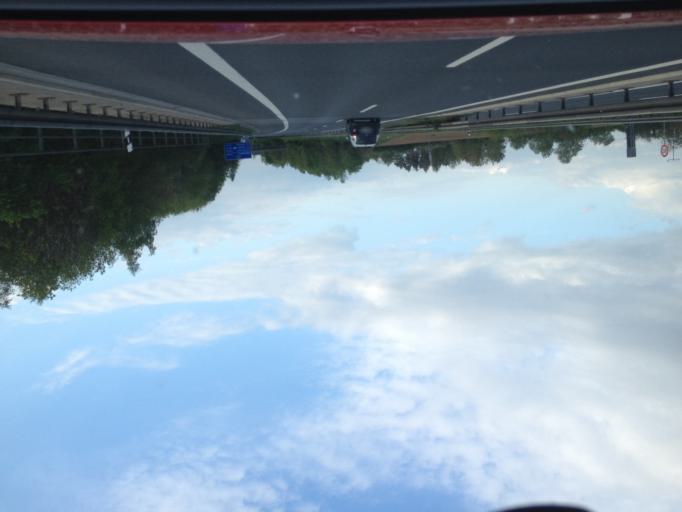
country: DE
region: Bavaria
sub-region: Upper Palatinate
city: Mitterteich
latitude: 49.9302
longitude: 12.2262
